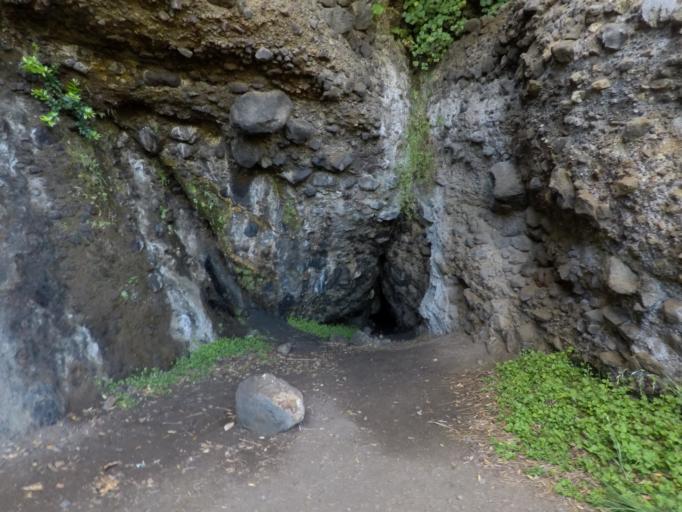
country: NZ
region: Auckland
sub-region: Auckland
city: Titirangi
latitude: -37.0408
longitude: 174.4998
